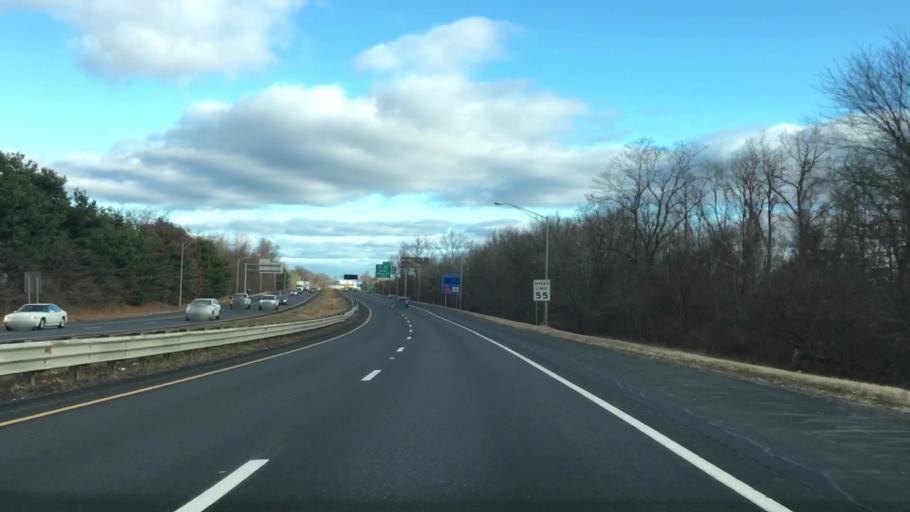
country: US
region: Massachusetts
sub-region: Hampden County
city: Springfield
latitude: 42.1317
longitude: -72.5579
